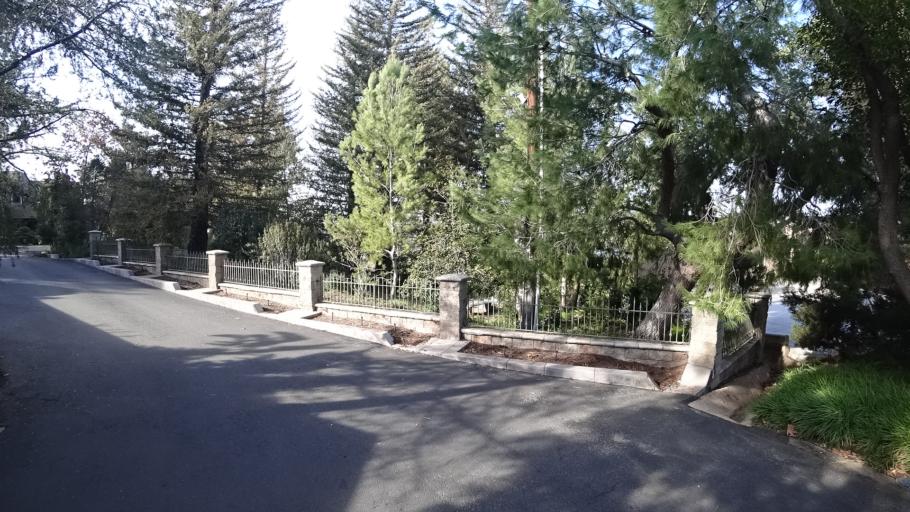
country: US
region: California
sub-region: Orange County
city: Yorba Linda
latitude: 33.8625
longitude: -117.7621
